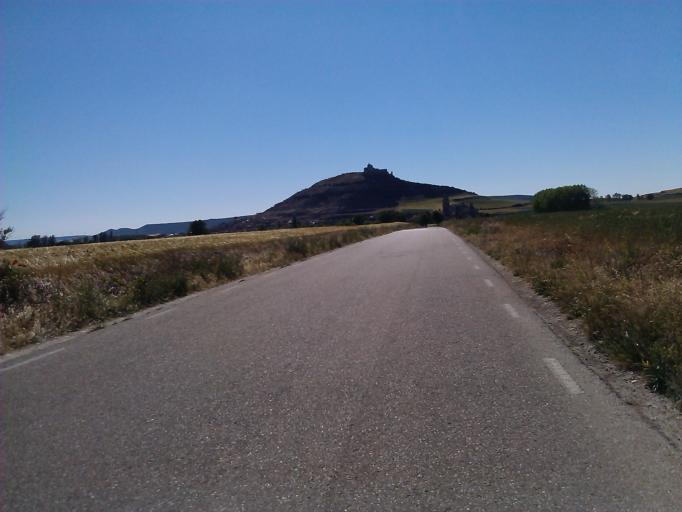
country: ES
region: Castille and Leon
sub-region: Provincia de Burgos
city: Villaquiran de la Puebla
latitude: 42.2920
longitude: -4.1175
